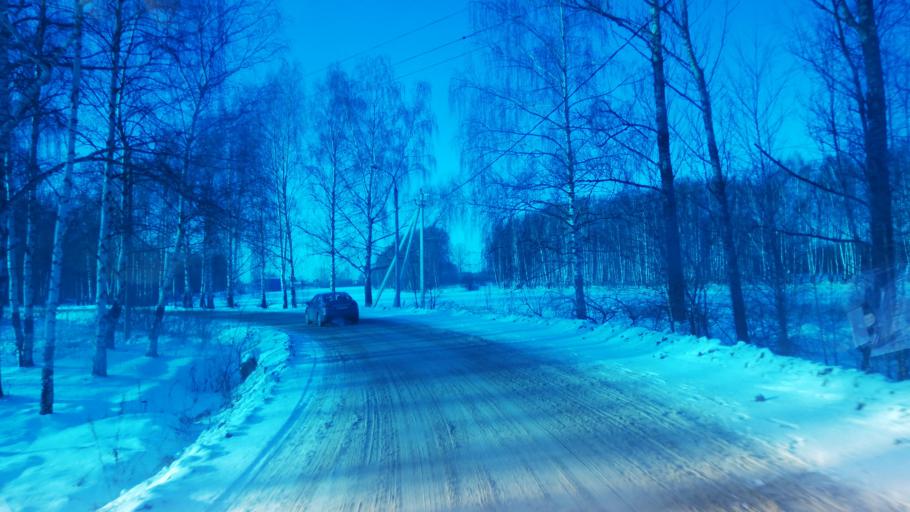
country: RU
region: Jaroslavl
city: Yaroslavl
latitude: 57.6202
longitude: 39.8127
